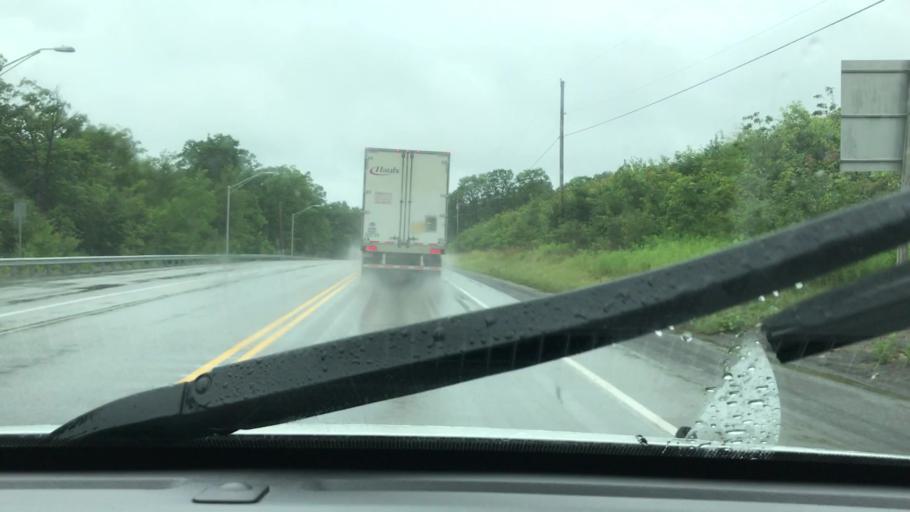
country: US
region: Pennsylvania
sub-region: Clearfield County
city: Osceola Mills
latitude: 40.7889
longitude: -78.2352
